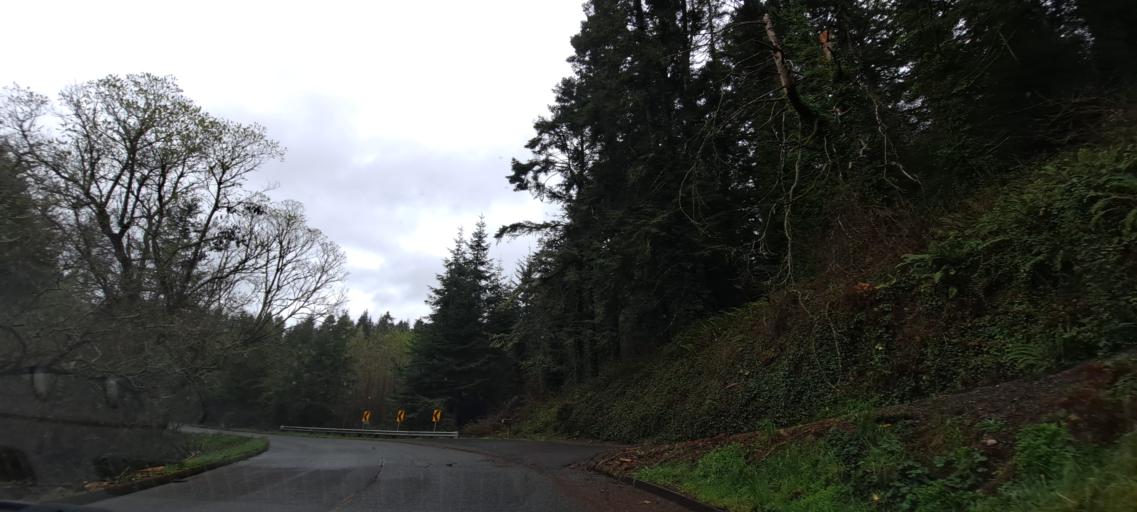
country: US
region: California
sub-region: Humboldt County
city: Fortuna
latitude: 40.5976
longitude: -124.1405
